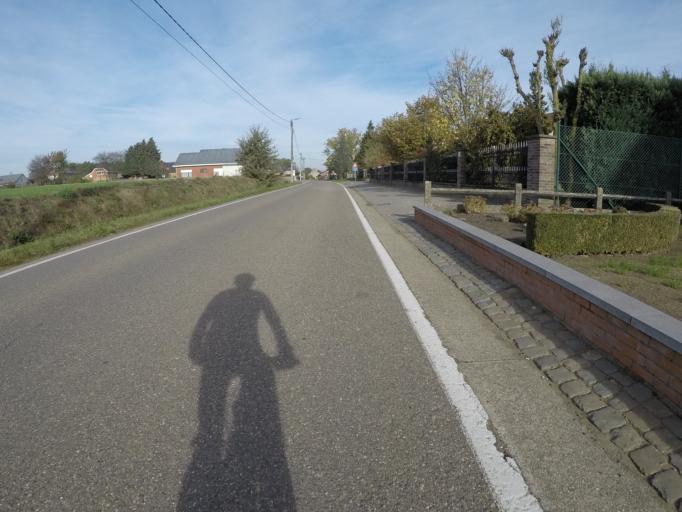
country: BE
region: Flanders
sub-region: Provincie Vlaams-Brabant
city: Begijnendijk
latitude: 50.9950
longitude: 4.7937
